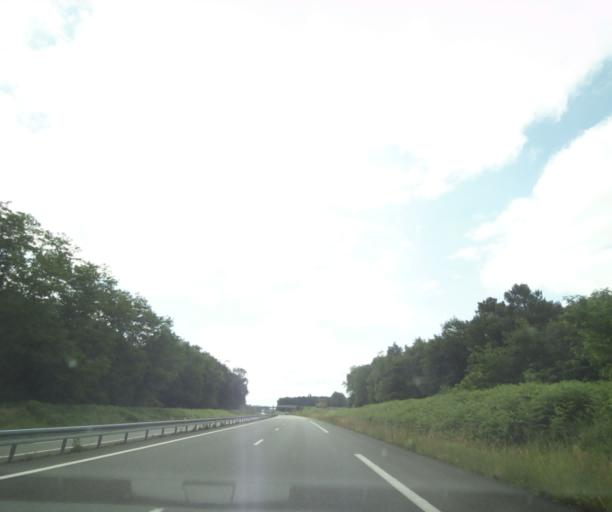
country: FR
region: Pays de la Loire
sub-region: Departement de Maine-et-Loire
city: Brion
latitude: 47.4328
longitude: -0.1636
